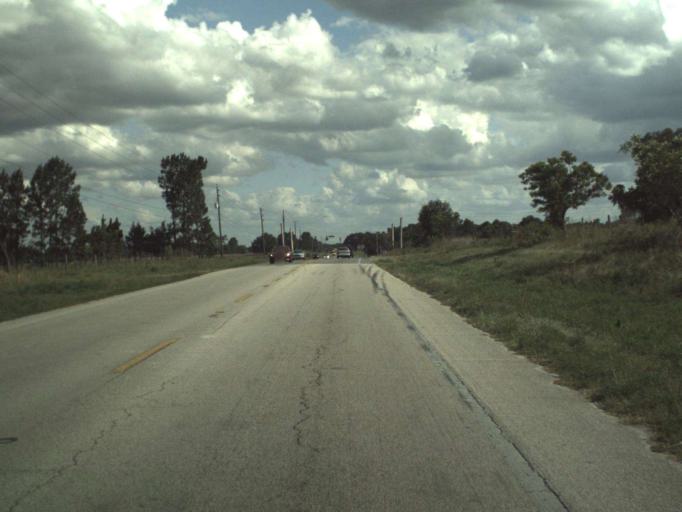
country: US
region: Florida
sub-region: Marion County
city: Belleview
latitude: 29.0892
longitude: -82.0536
